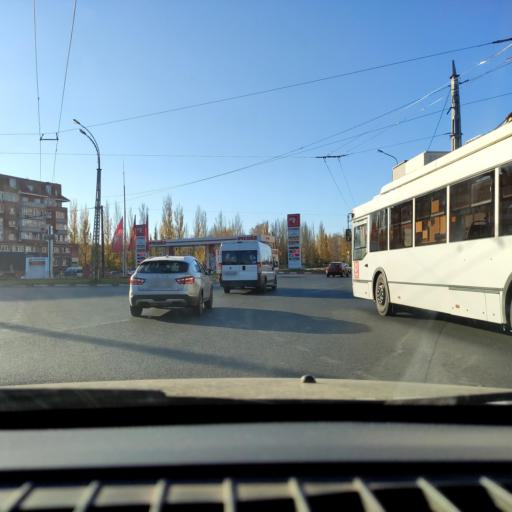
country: RU
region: Samara
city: Tol'yatti
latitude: 53.5170
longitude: 49.3088
